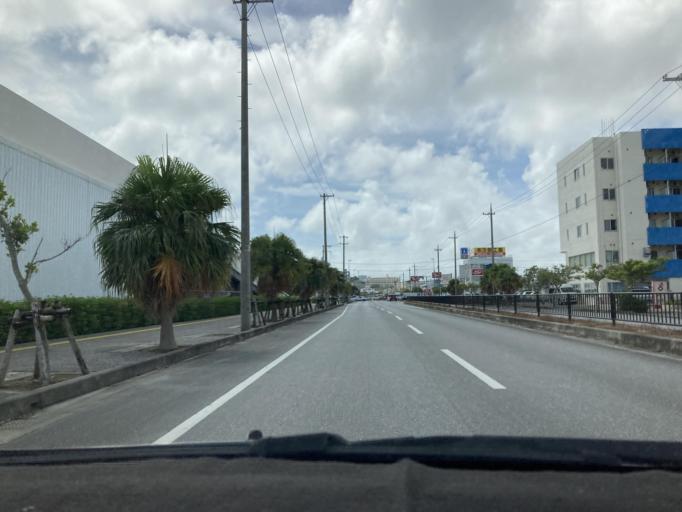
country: JP
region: Okinawa
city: Ginowan
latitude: 26.2070
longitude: 127.7629
